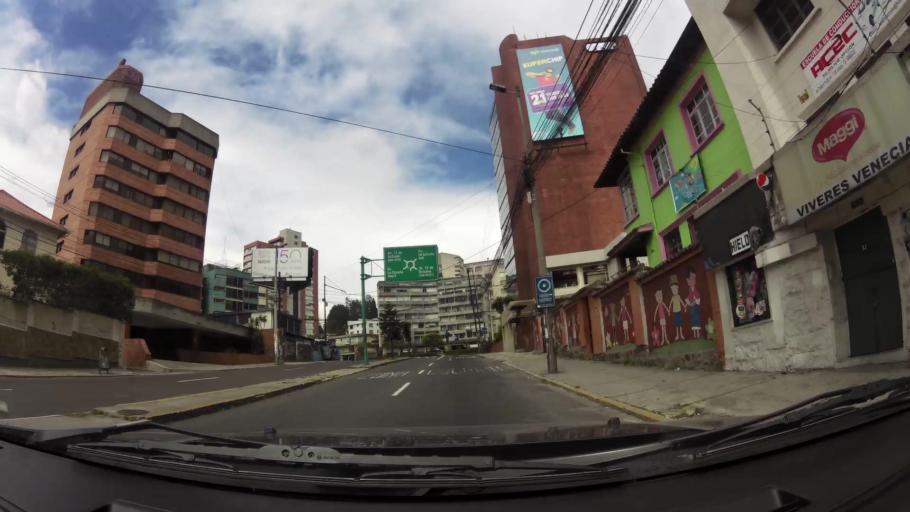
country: EC
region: Pichincha
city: Quito
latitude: -0.2033
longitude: -78.4837
